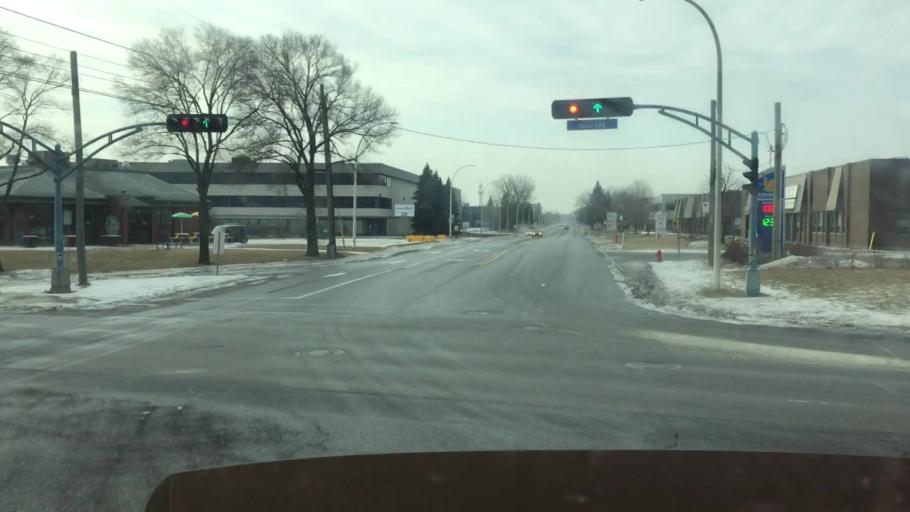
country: CA
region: Quebec
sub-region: Montreal
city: Pointe-Claire
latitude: 45.4765
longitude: -73.7897
